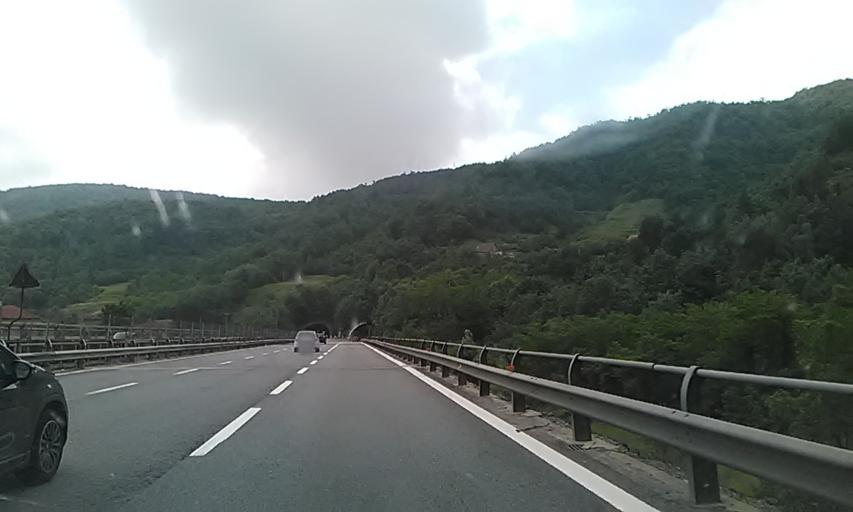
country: IT
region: Liguria
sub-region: Provincia di Genova
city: Masone
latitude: 44.4930
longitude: 8.7312
